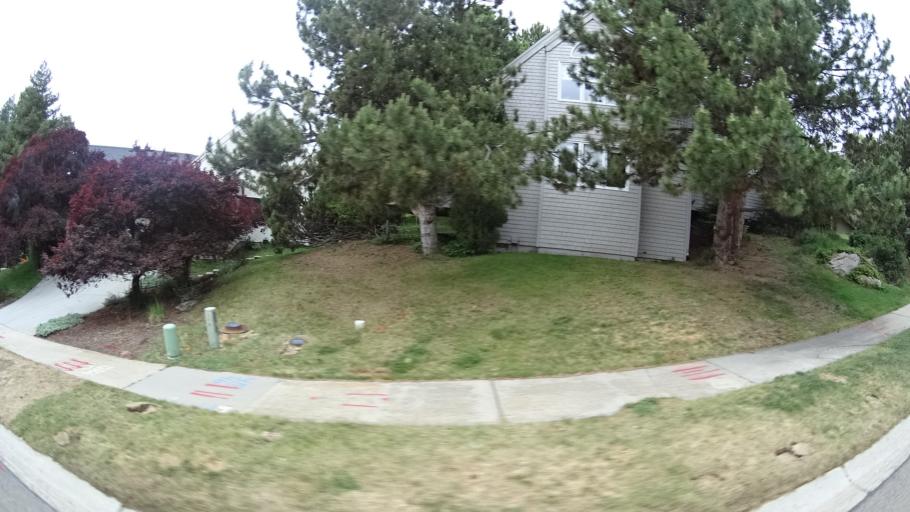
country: US
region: Idaho
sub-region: Ada County
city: Boise
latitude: 43.6131
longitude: -116.1697
